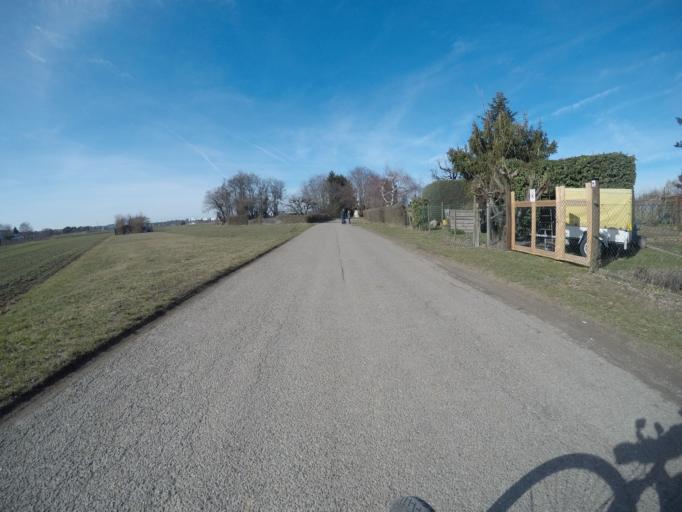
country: DE
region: Baden-Wuerttemberg
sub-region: Regierungsbezirk Stuttgart
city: Leinfelden-Echterdingen
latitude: 48.7345
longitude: 9.1402
